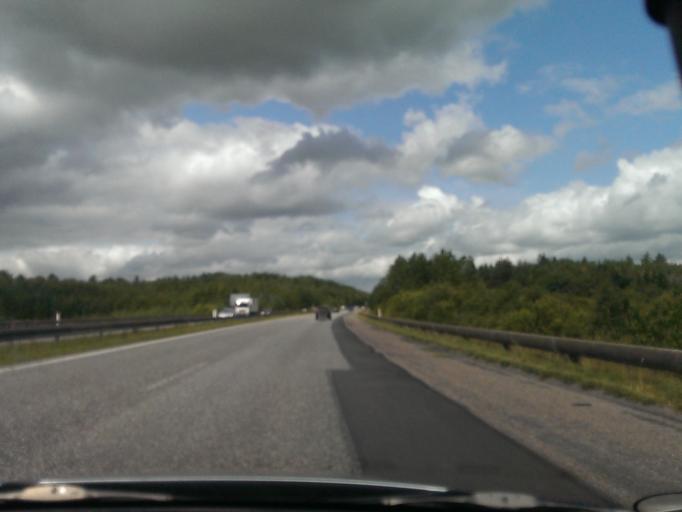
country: DK
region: North Denmark
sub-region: Mariagerfjord Kommune
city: Hobro
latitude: 56.5810
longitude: 9.7999
